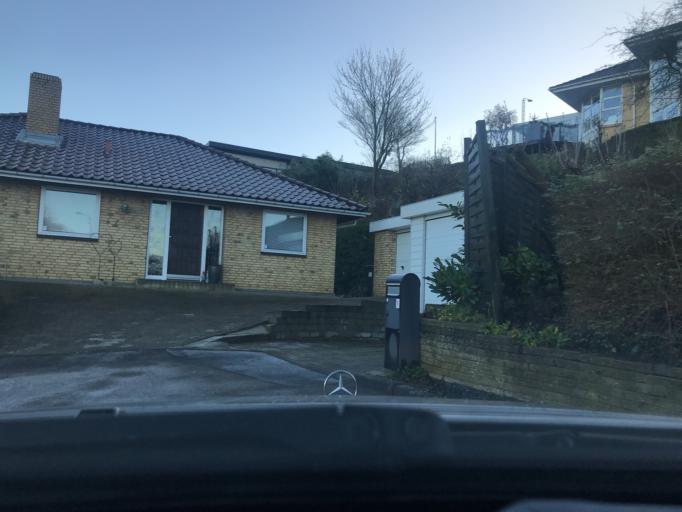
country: DK
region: South Denmark
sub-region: Sonderborg Kommune
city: Dybbol
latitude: 54.9166
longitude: 9.7647
